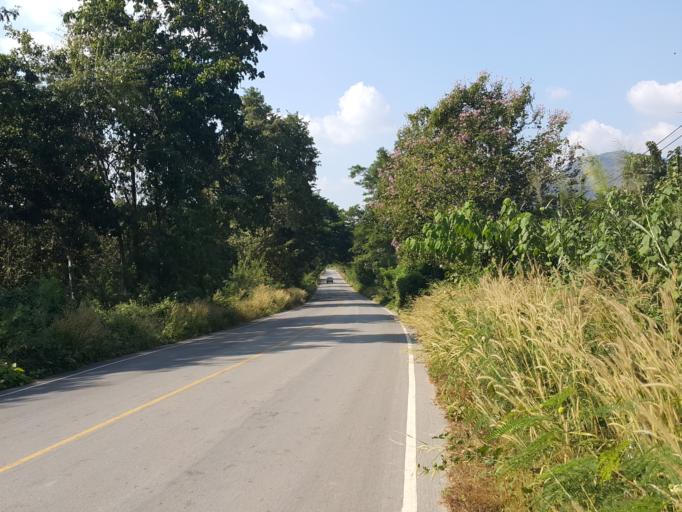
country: TH
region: Sukhothai
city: Thung Saliam
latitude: 17.3391
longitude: 99.4743
